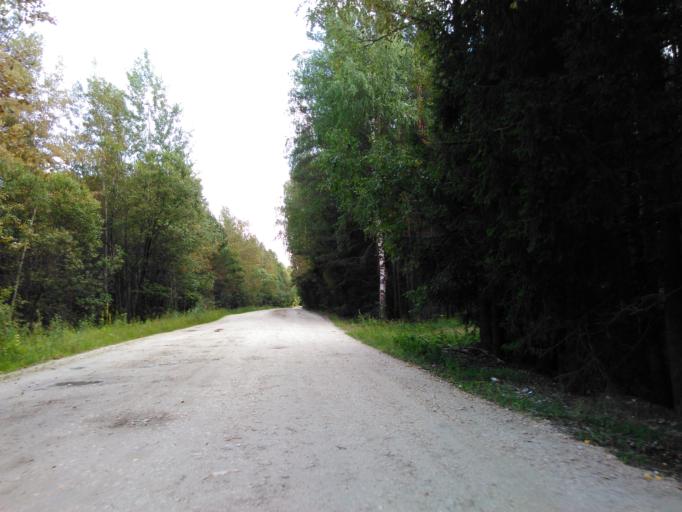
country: RU
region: Vladimir
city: Krasnyy Oktyabr'
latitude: 56.0103
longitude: 38.8179
